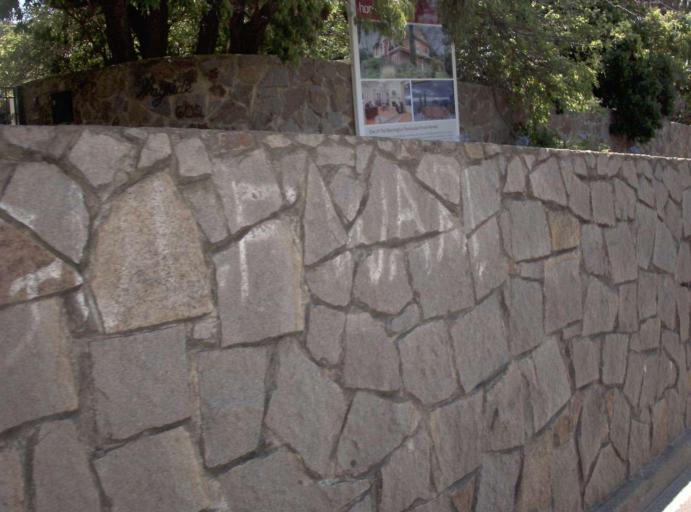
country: AU
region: Victoria
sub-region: Frankston
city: Frankston
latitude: -38.1566
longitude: 145.1056
